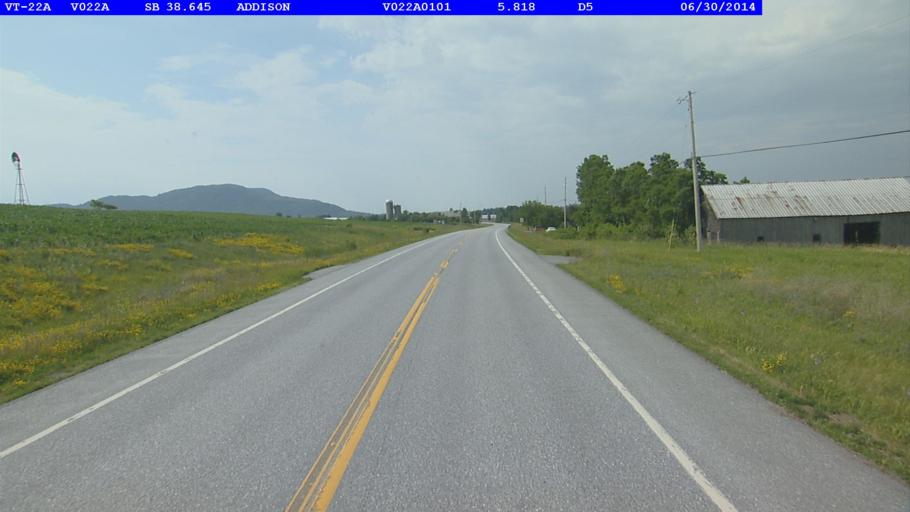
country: US
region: Vermont
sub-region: Addison County
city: Vergennes
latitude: 44.1124
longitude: -73.2939
